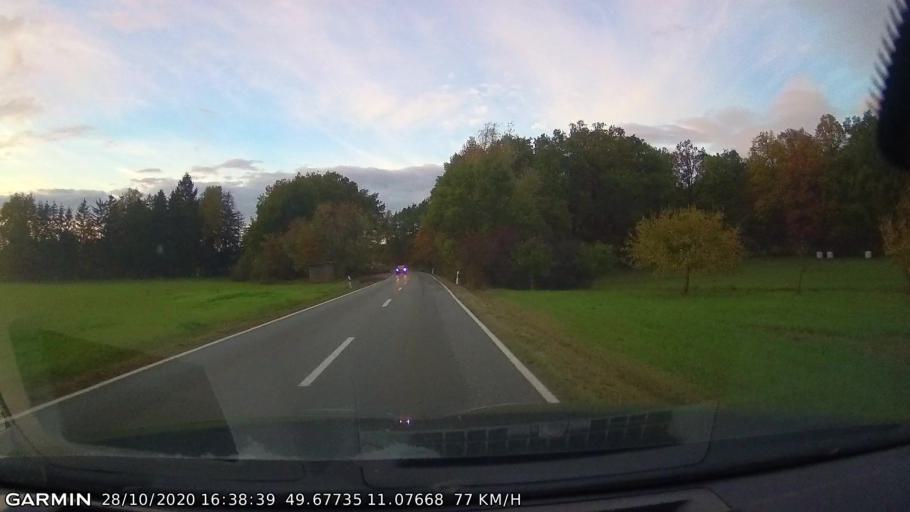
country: DE
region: Bavaria
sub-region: Upper Franconia
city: Poxdorf
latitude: 49.6775
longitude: 11.0765
